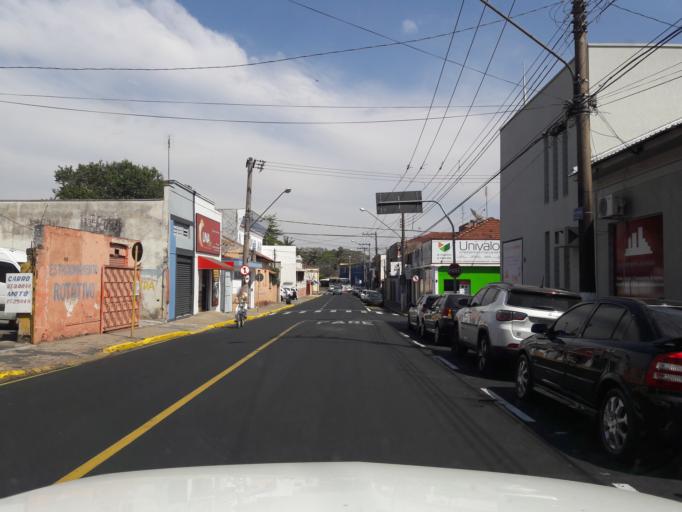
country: BR
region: Sao Paulo
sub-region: Moji-Guacu
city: Mogi-Gaucu
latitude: -22.3704
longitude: -46.9394
